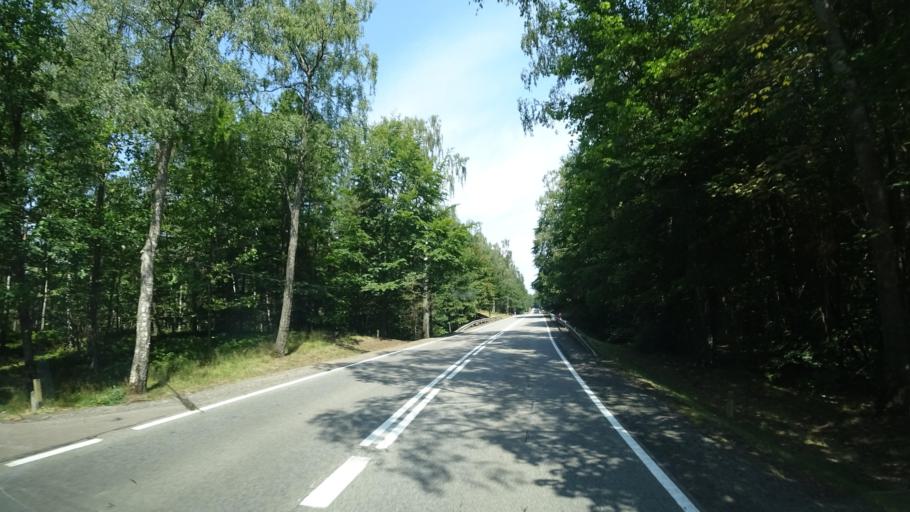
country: PL
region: Pomeranian Voivodeship
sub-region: Powiat koscierski
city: Grabowo Koscierskie
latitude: 54.2120
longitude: 18.1145
